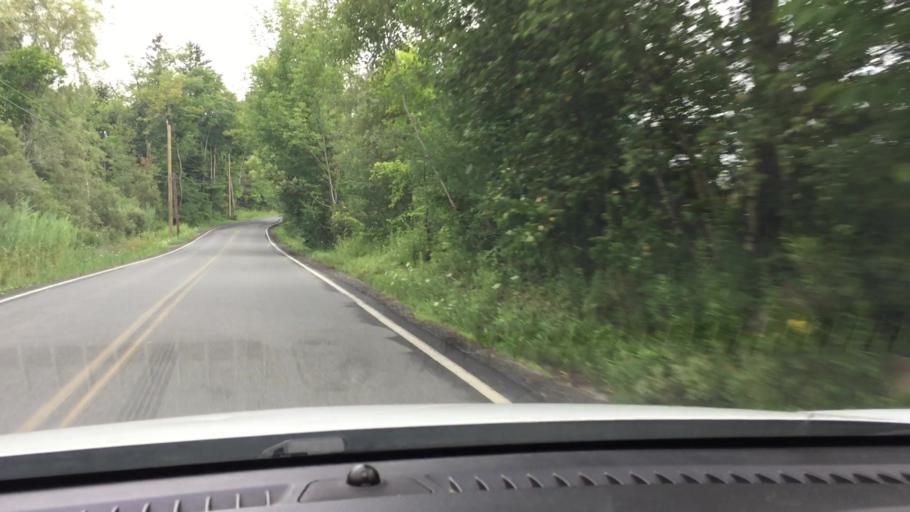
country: US
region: Massachusetts
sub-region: Berkshire County
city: Hinsdale
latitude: 42.4423
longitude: -73.1376
